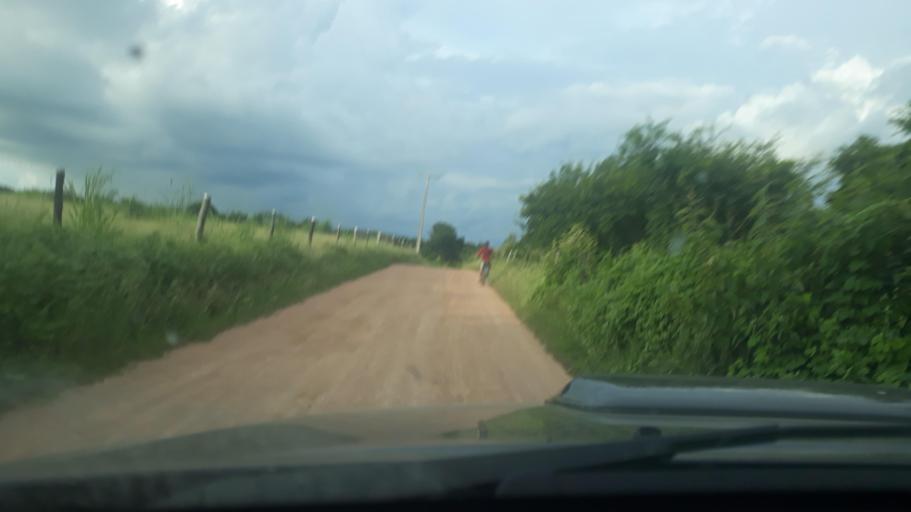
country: BR
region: Bahia
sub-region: Riacho De Santana
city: Riacho de Santana
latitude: -13.9006
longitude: -43.0021
